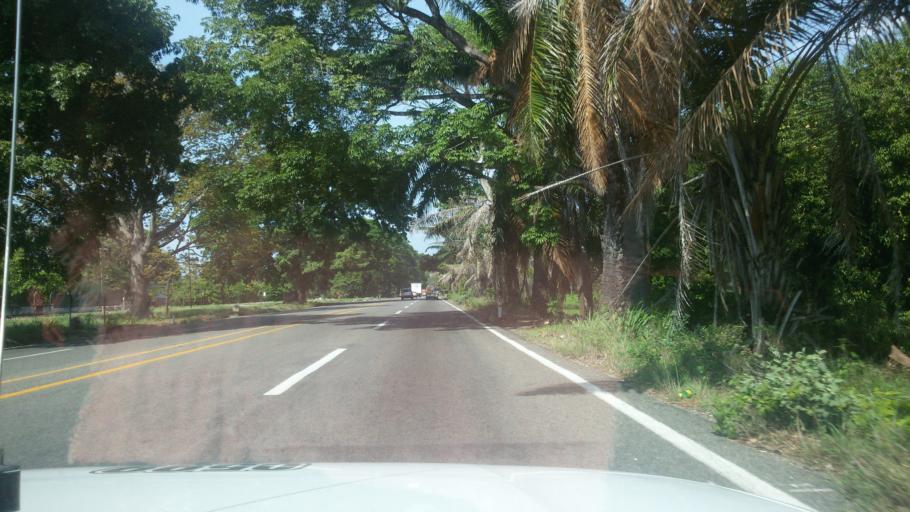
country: MX
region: Chiapas
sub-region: Tapachula
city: Congregacion Reforma
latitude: 14.8247
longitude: -92.3349
